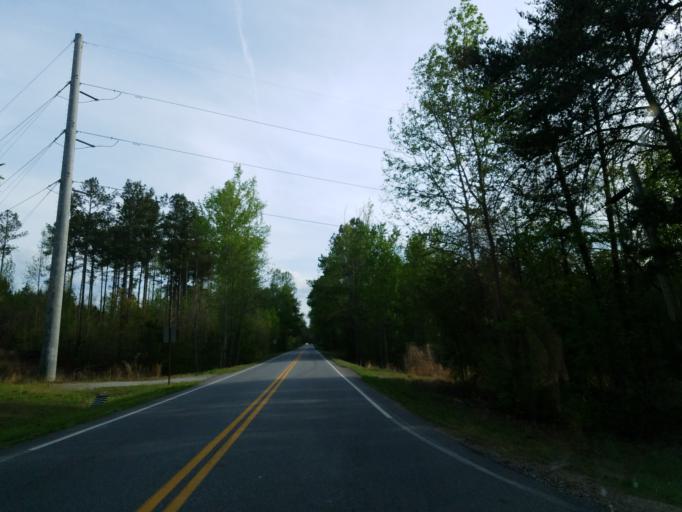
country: US
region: Georgia
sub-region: Cherokee County
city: Ball Ground
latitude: 34.3294
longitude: -84.2653
